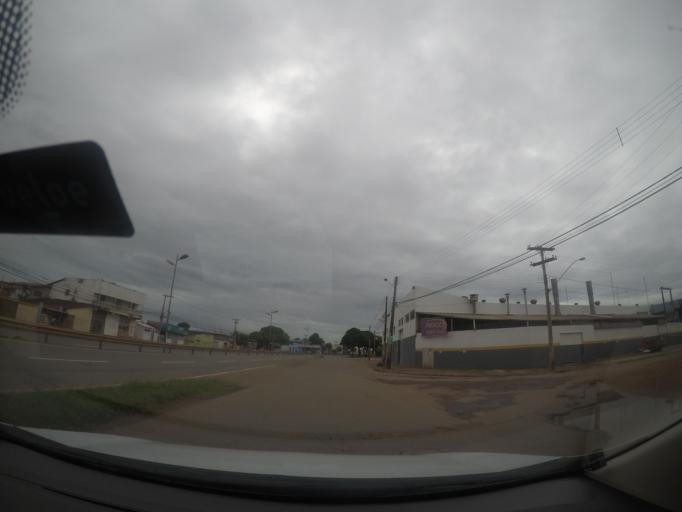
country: BR
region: Goias
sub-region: Goiania
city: Goiania
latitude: -16.6501
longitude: -49.3241
